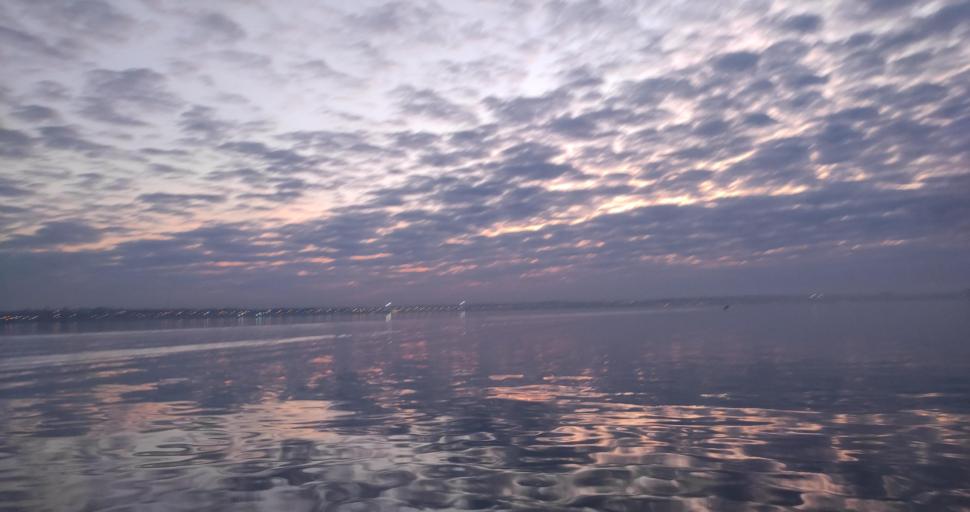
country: AR
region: Misiones
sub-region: Departamento de Capital
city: Posadas
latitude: -27.4187
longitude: -55.8537
